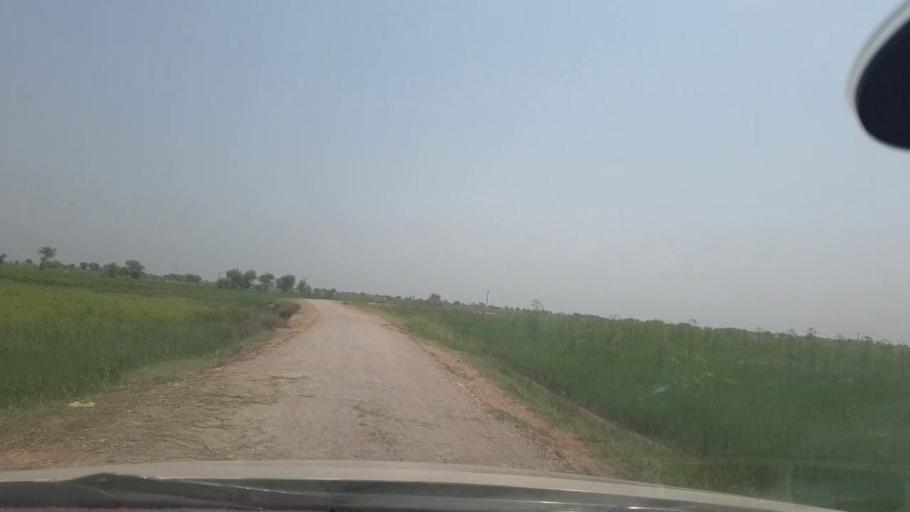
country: PK
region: Sindh
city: Jacobabad
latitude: 28.1700
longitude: 68.3914
